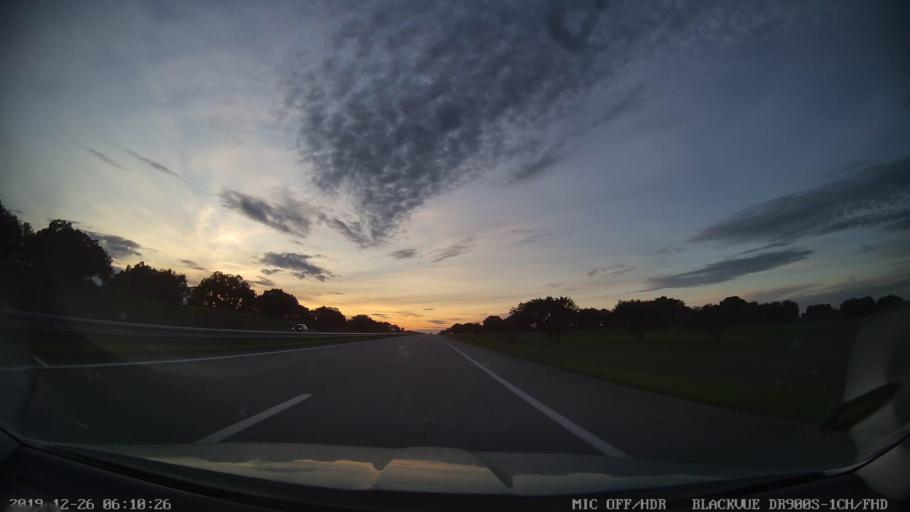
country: PT
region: Evora
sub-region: Montemor-O-Novo
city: Montemor-o-Novo
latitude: 38.6722
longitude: -8.1929
